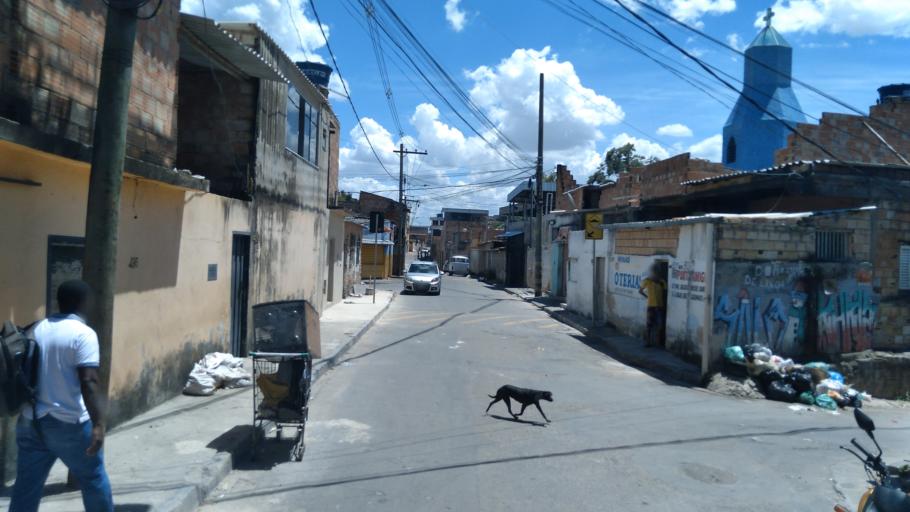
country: BR
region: Minas Gerais
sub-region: Santa Luzia
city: Santa Luzia
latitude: -19.8341
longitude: -43.8939
